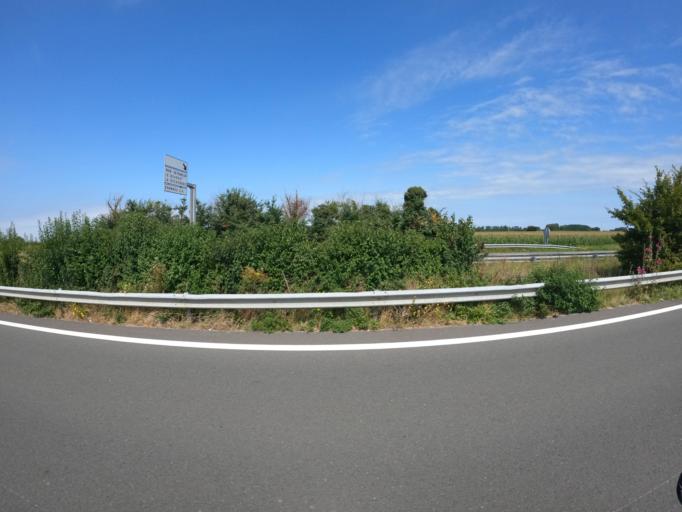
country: FR
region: Poitou-Charentes
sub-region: Departement des Deux-Sevres
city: Frontenay-Rohan-Rohan
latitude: 46.2231
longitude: -0.6001
